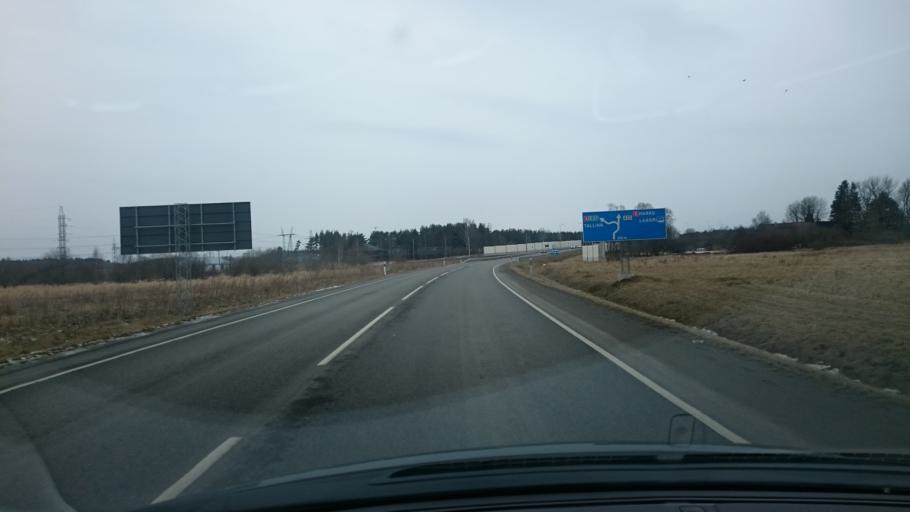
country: EE
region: Harju
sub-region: Saue vald
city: Laagri
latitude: 59.3341
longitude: 24.6175
